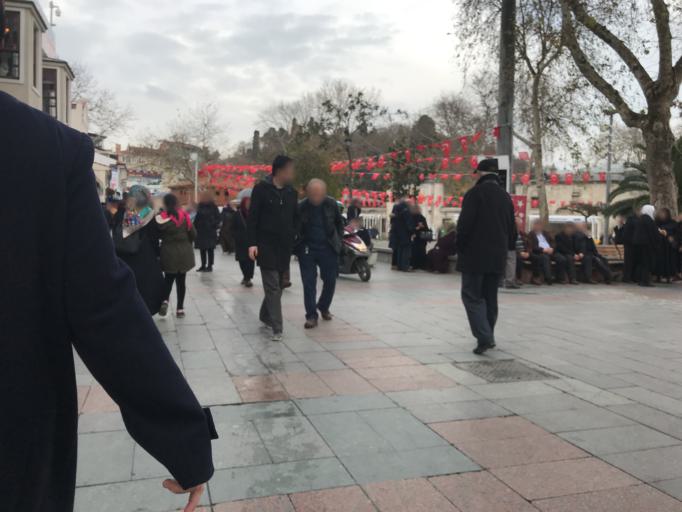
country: TR
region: Istanbul
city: Istanbul
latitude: 41.0471
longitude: 28.9333
